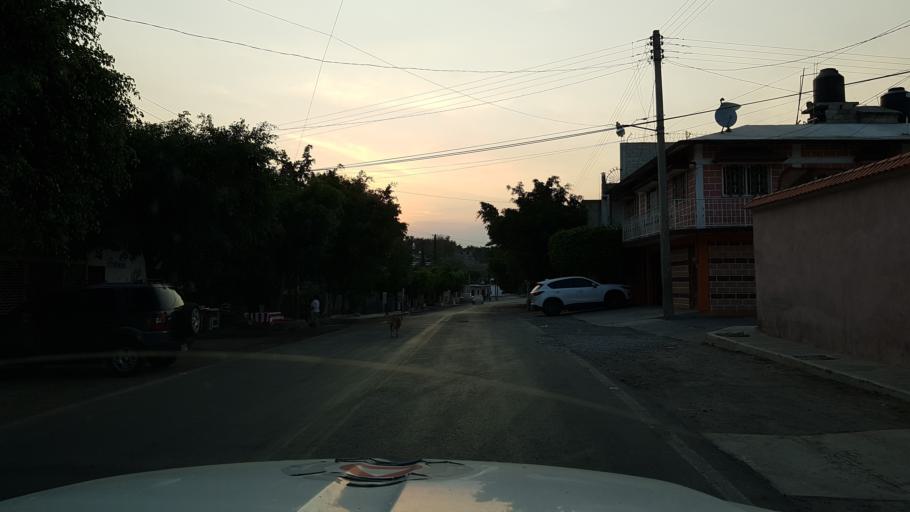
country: MX
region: Morelos
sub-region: Ayala
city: Abelardo L. Rodriguez
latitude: 18.7252
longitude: -98.9970
